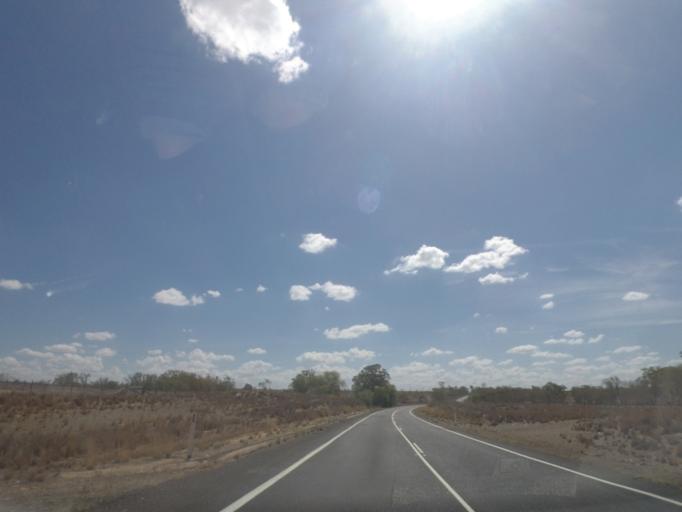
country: AU
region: Queensland
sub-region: Southern Downs
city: Warwick
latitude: -28.2056
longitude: 151.5833
